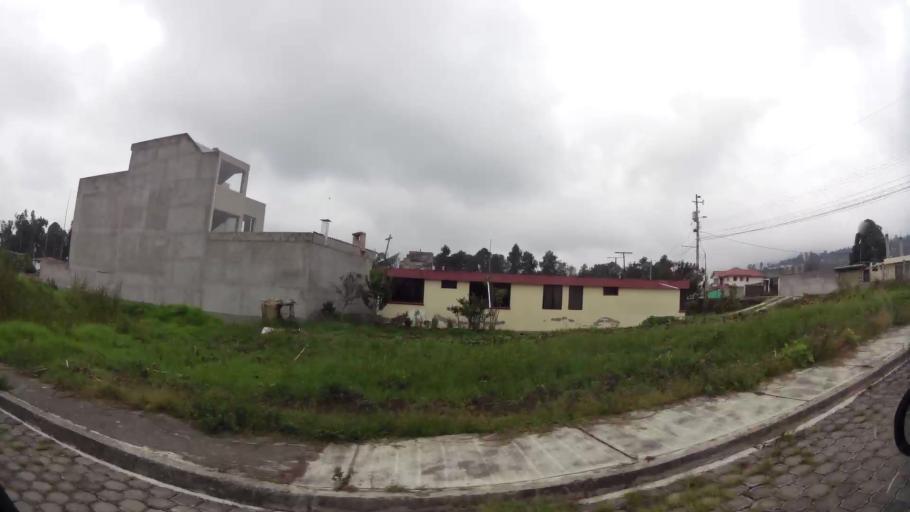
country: EC
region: Pichincha
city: Quito
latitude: -0.2684
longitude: -78.4742
